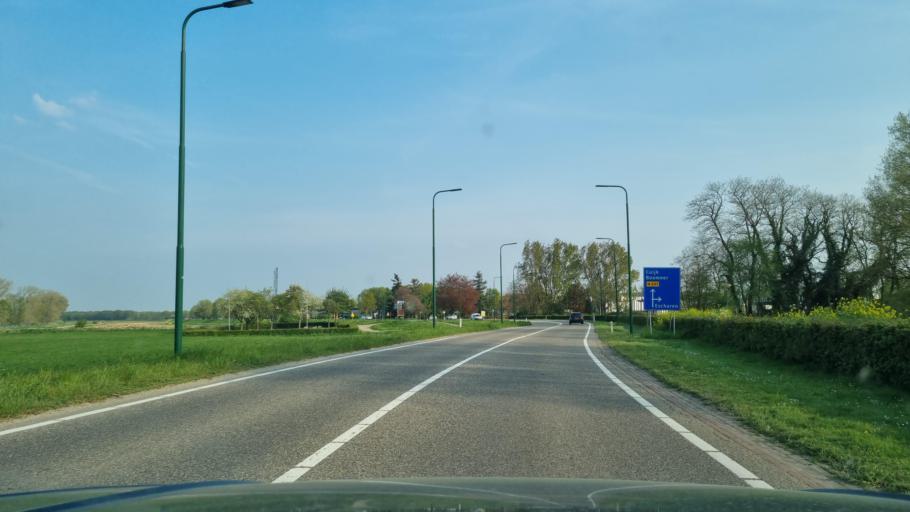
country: NL
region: North Brabant
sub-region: Gemeente Grave
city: Grave
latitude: 51.7572
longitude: 5.7436
